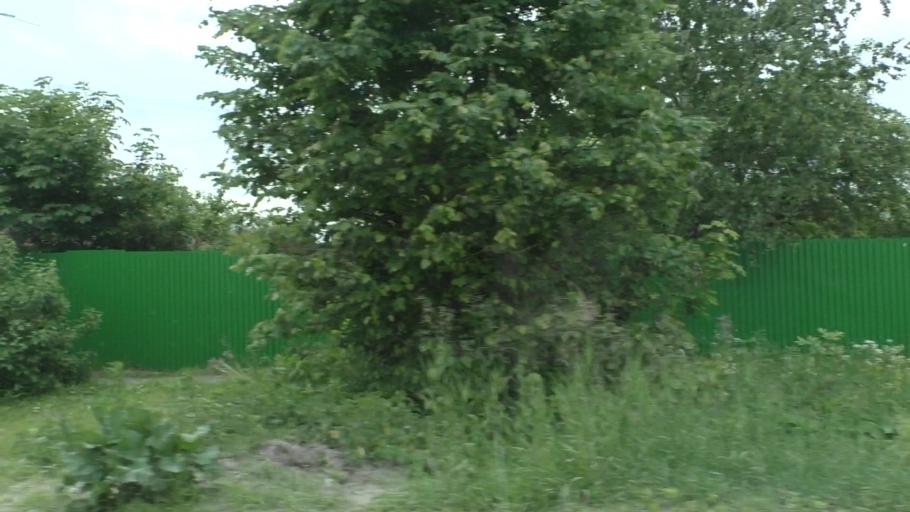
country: RU
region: Moskovskaya
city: Imeni Tsyurupy
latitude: 55.5040
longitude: 38.7809
